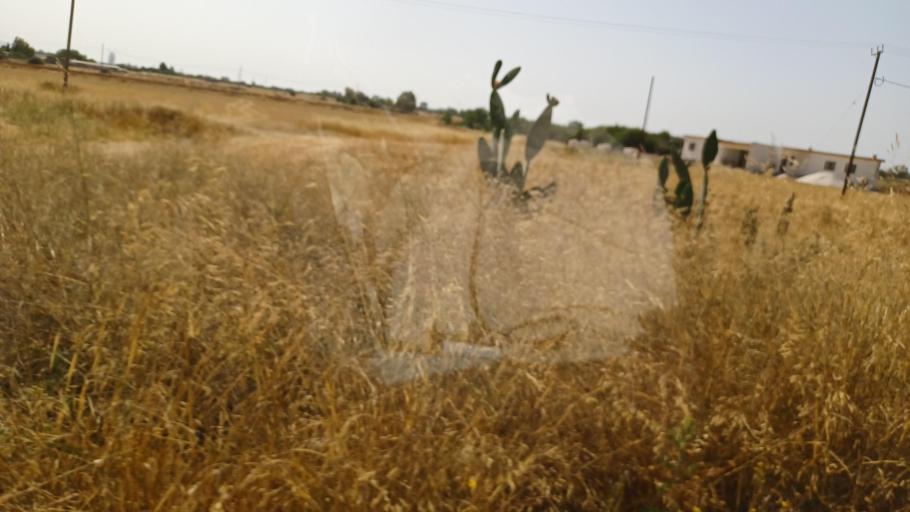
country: CY
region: Ammochostos
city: Liopetri
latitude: 34.9832
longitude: 33.8821
